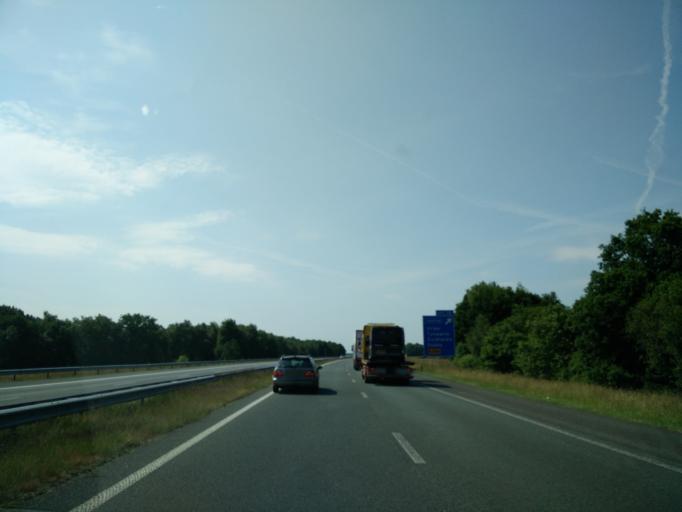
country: NL
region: Drenthe
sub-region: Gemeente Tynaarlo
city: Tynaarlo
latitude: 53.0974
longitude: 6.6111
